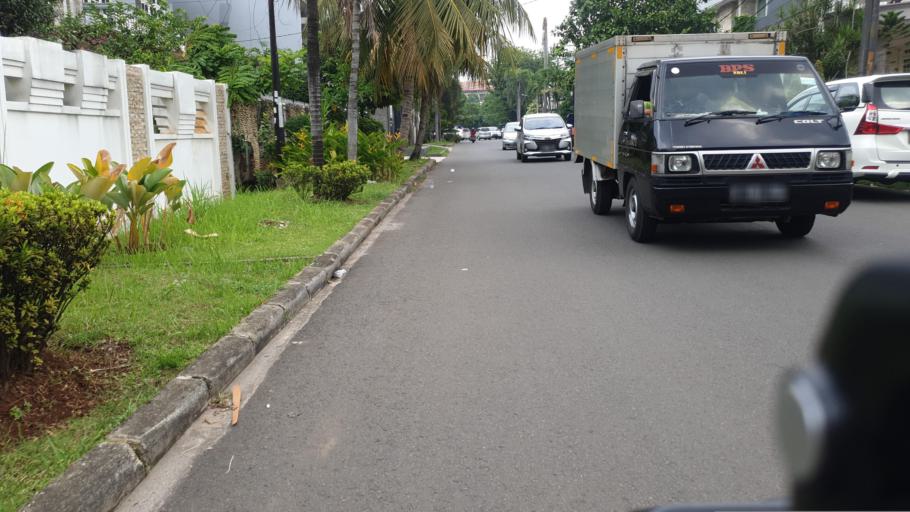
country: ID
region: West Java
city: Ciputat
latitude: -6.1932
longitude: 106.7507
